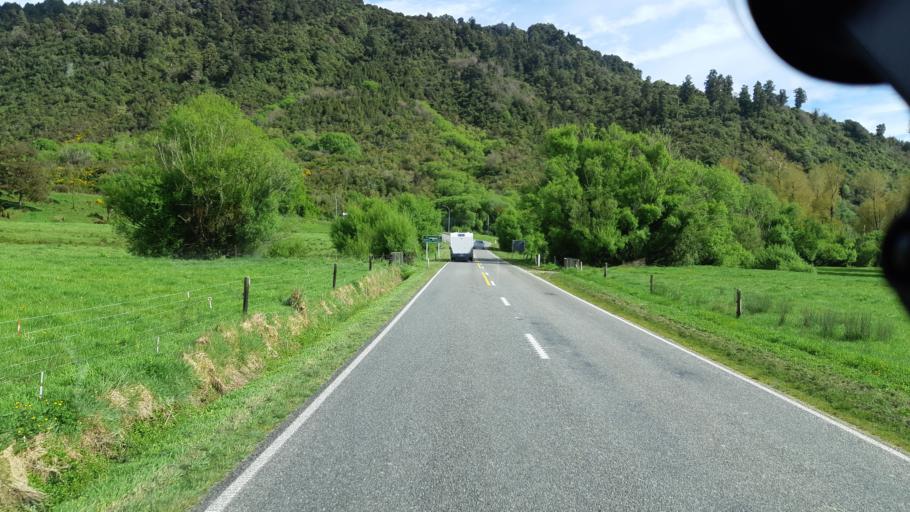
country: NZ
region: West Coast
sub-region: Buller District
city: Westport
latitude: -41.8596
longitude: 171.9391
